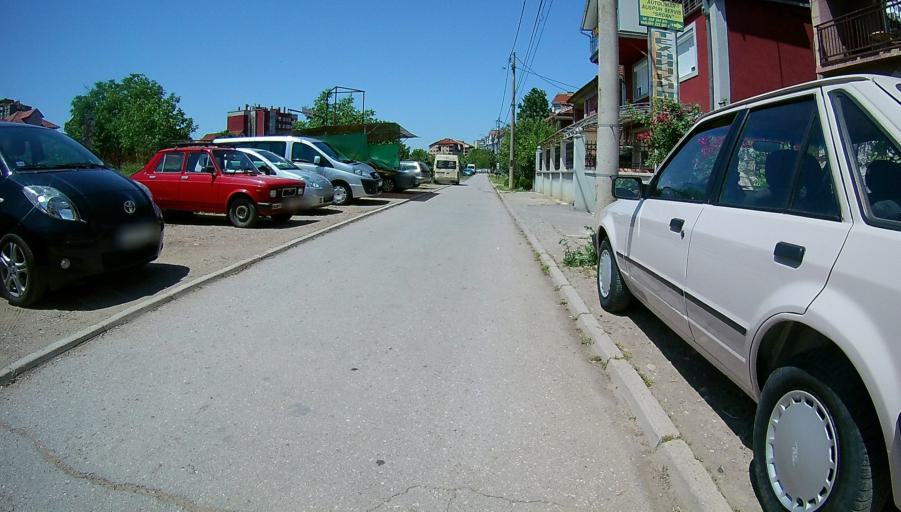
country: RS
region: Central Serbia
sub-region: Nisavski Okrug
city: Nis
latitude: 43.3130
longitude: 21.9023
